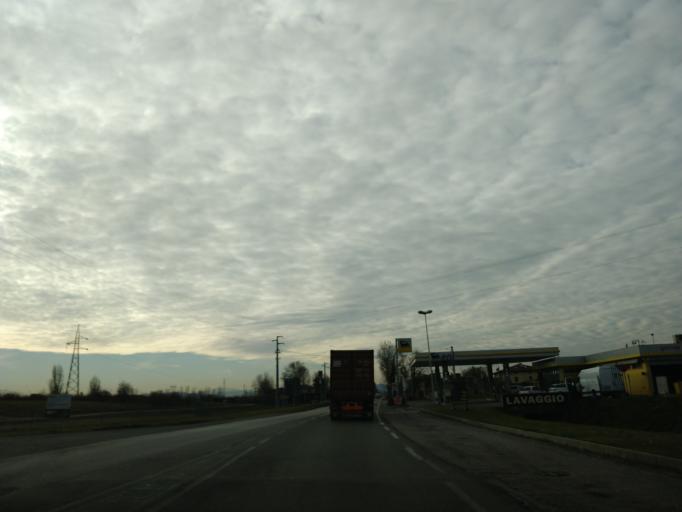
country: IT
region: Emilia-Romagna
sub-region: Provincia di Bologna
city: Castel Maggiore
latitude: 44.5848
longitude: 11.3896
